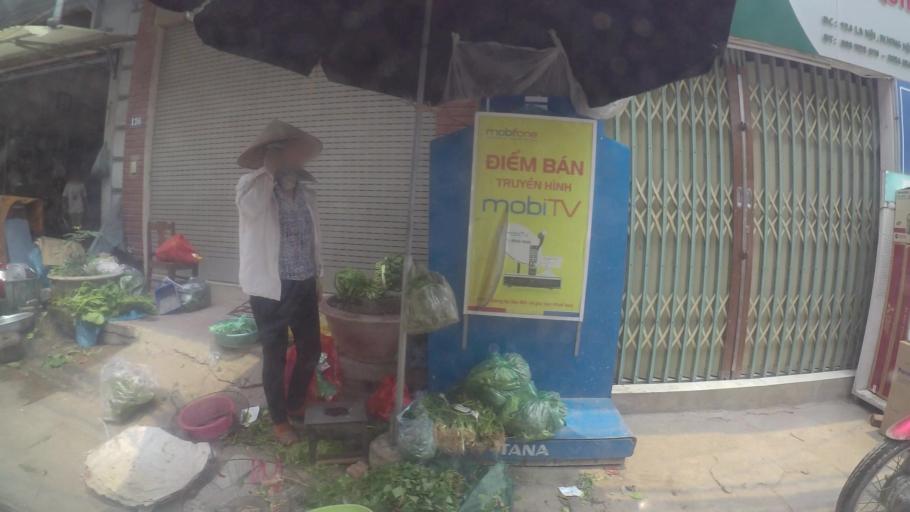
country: VN
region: Ha Noi
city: Ha Dong
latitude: 20.9820
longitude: 105.7487
